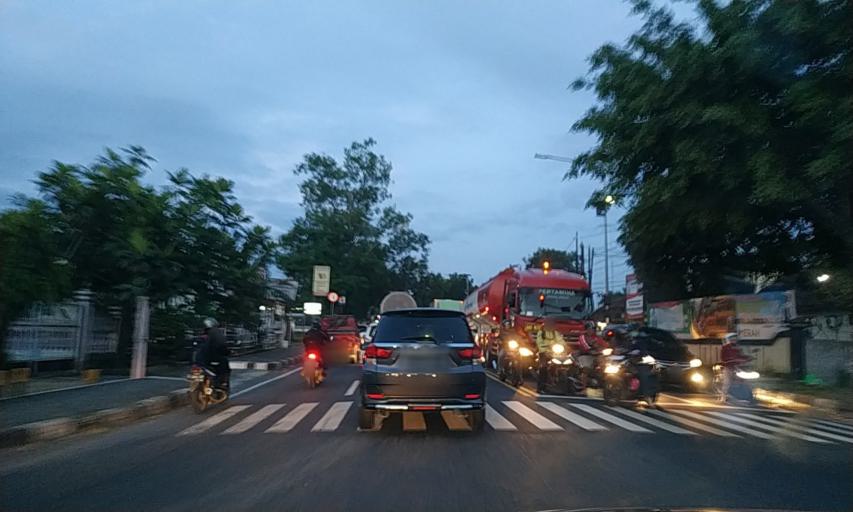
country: ID
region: Daerah Istimewa Yogyakarta
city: Godean
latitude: -7.8268
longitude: 110.2246
